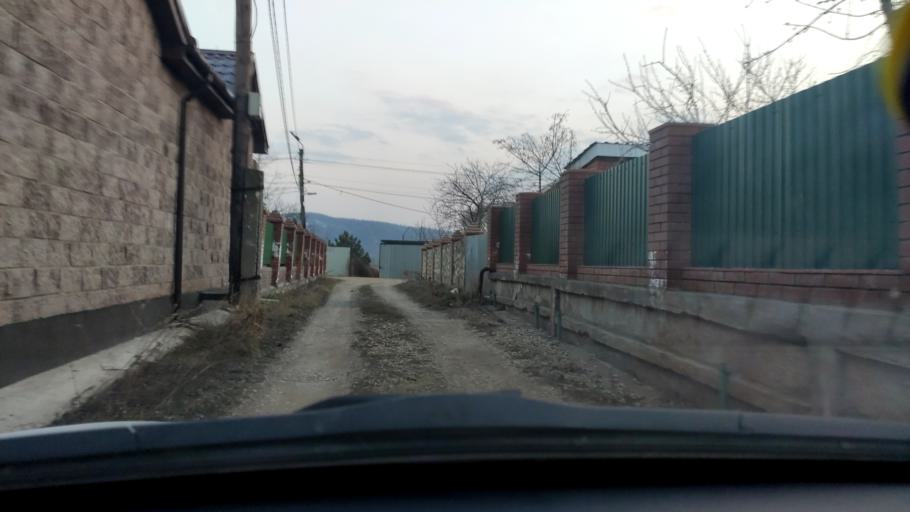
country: RU
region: Samara
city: Zhigulevsk
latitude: 53.4517
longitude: 49.5244
